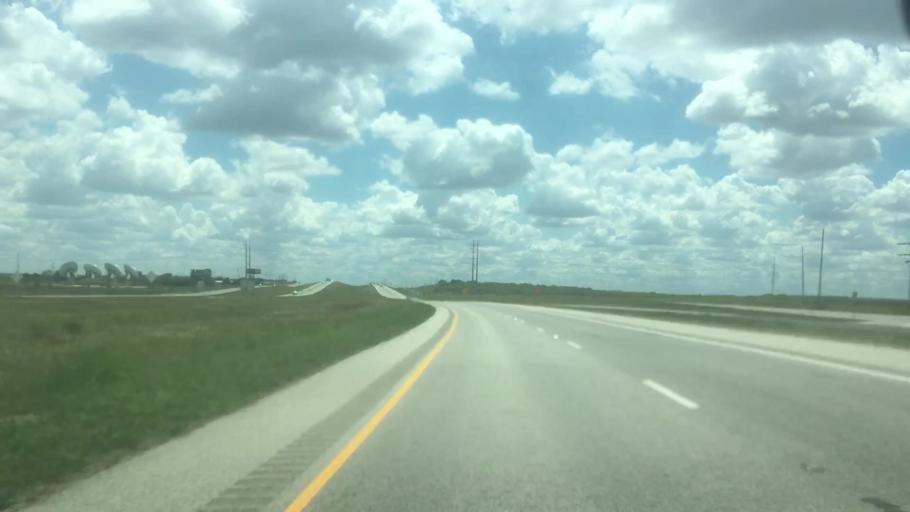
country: US
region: Texas
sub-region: Caldwell County
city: Uhland
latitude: 30.0152
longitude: -97.6884
